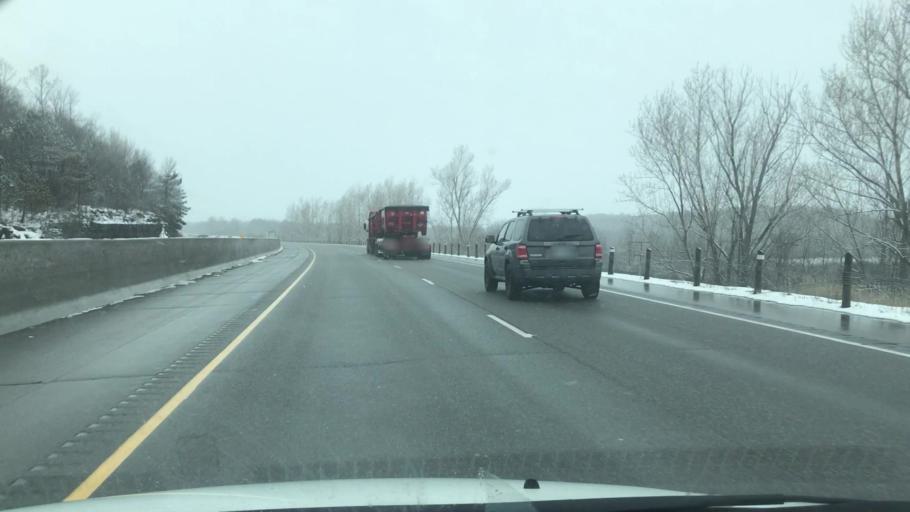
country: CA
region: Ontario
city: Kingston
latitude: 44.3160
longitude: -76.3810
